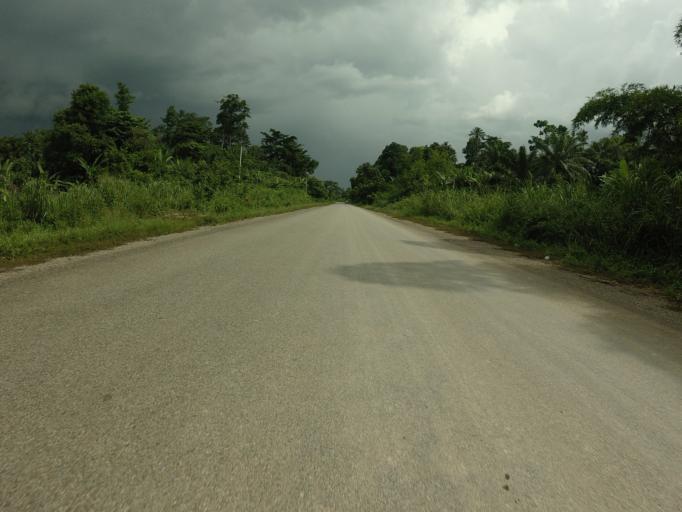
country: TG
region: Plateaux
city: Badou
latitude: 7.6840
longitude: 0.5225
